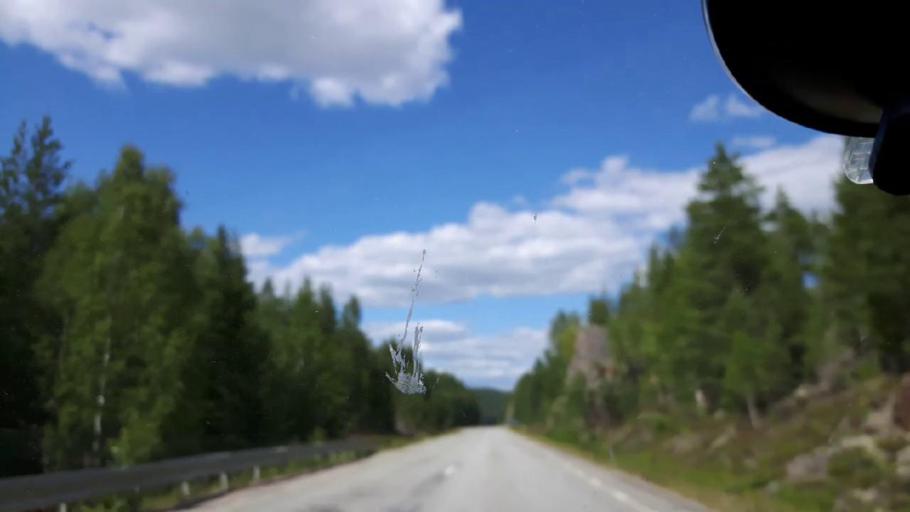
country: SE
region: Vaesternorrland
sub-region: Ange Kommun
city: Fransta
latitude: 62.7748
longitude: 16.2432
